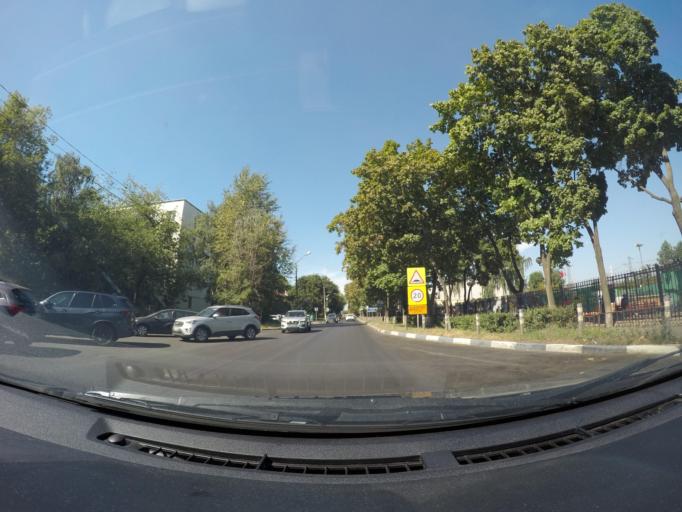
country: RU
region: Moscow
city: Nekrasovka
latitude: 55.6695
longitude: 37.9195
